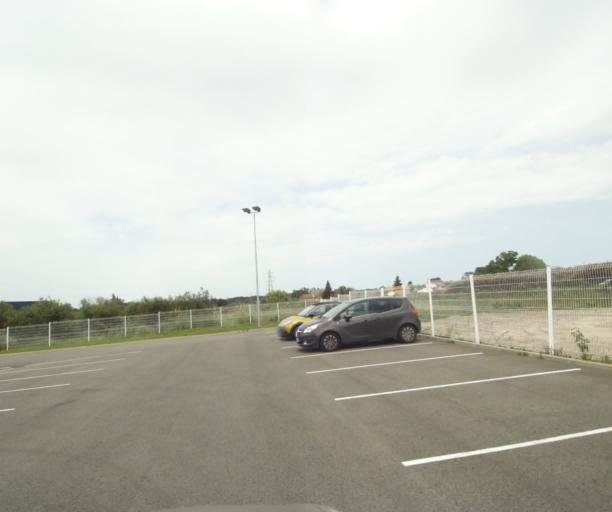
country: FR
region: Aquitaine
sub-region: Departement des Pyrenees-Atlantiques
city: Mouguerre
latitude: 43.4898
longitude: -1.4201
